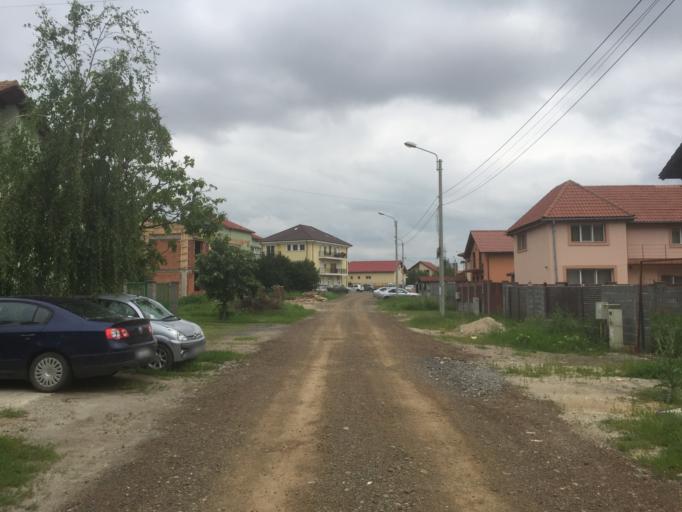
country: RO
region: Timis
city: Timisoara
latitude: 45.7554
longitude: 21.1956
